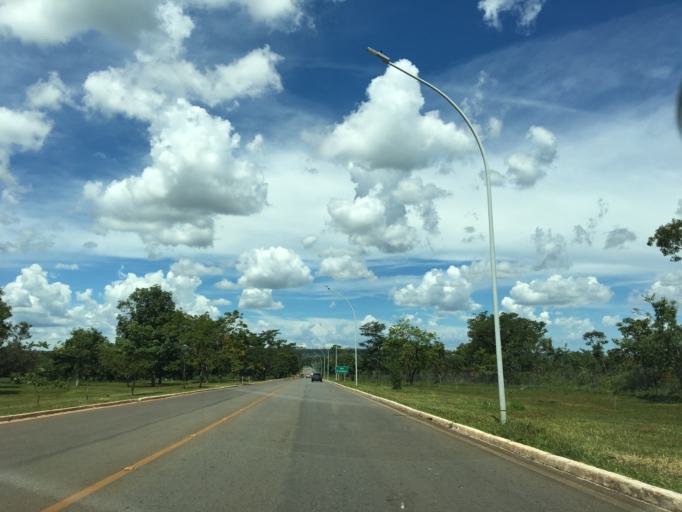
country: BR
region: Federal District
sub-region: Brasilia
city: Brasilia
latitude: -15.7987
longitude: -47.8436
